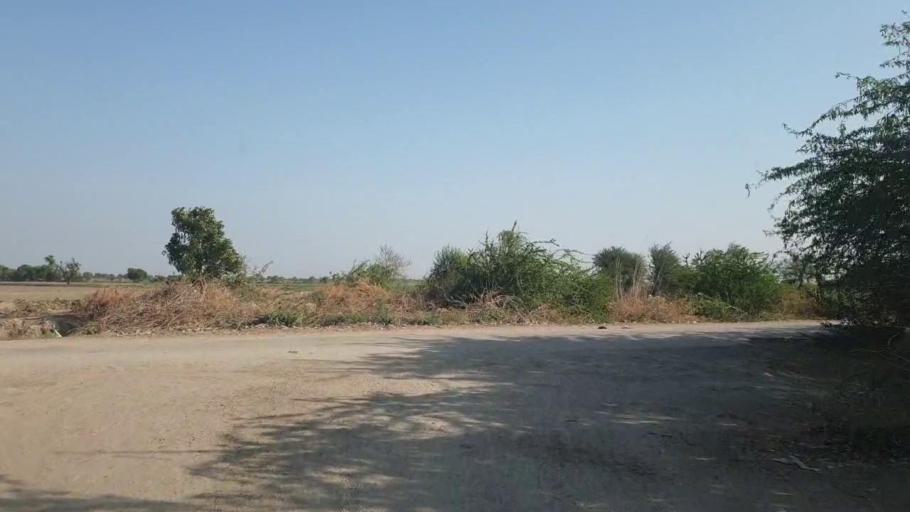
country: PK
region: Sindh
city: Chor
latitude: 25.5140
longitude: 69.6800
